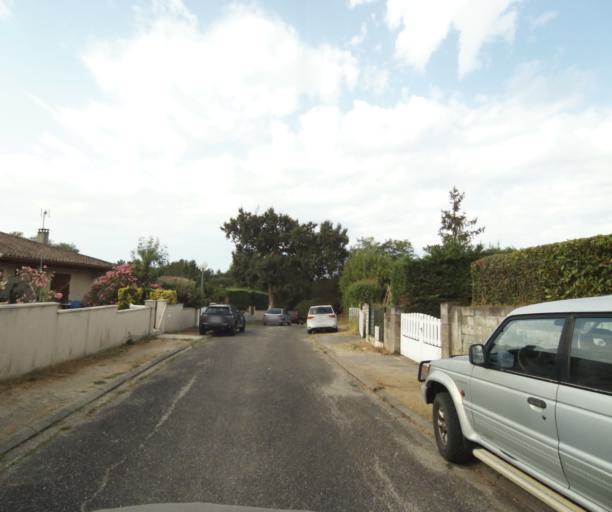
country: FR
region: Aquitaine
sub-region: Departement de la Gironde
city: Creon
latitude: 44.7674
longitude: -0.3547
